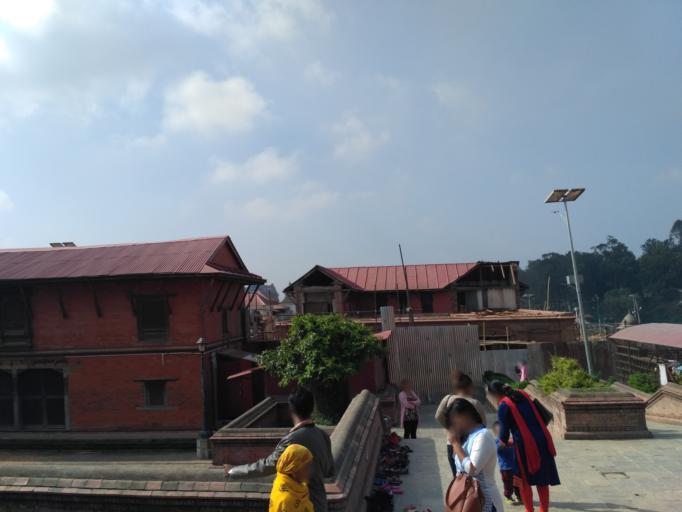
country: NP
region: Central Region
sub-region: Bagmati Zone
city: Kathmandu
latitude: 27.7111
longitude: 85.3478
